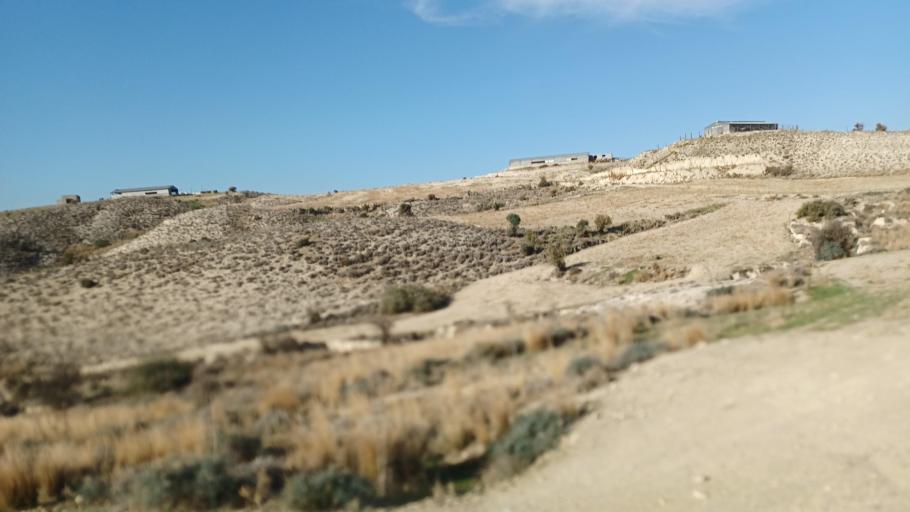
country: CY
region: Larnaka
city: Psevdas
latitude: 34.9471
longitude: 33.5166
